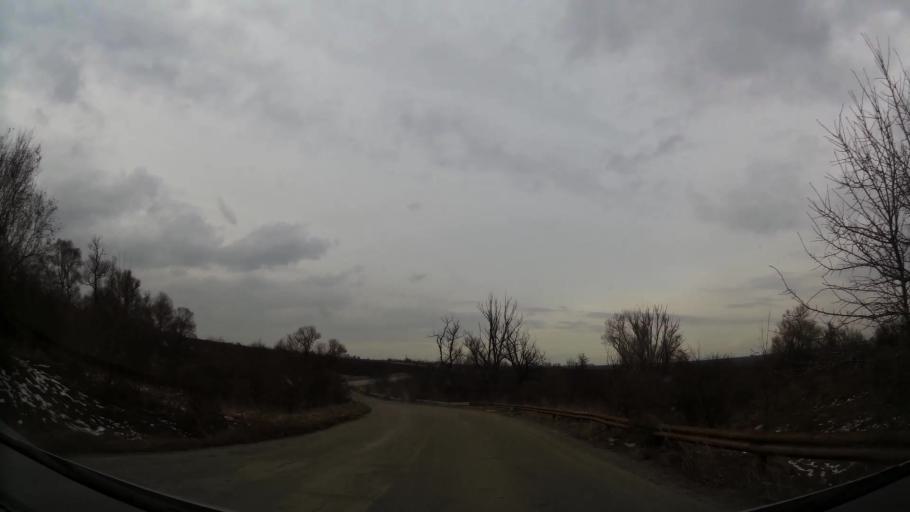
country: BG
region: Sofiya
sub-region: Obshtina Bozhurishte
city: Bozhurishte
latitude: 42.7025
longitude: 23.2203
